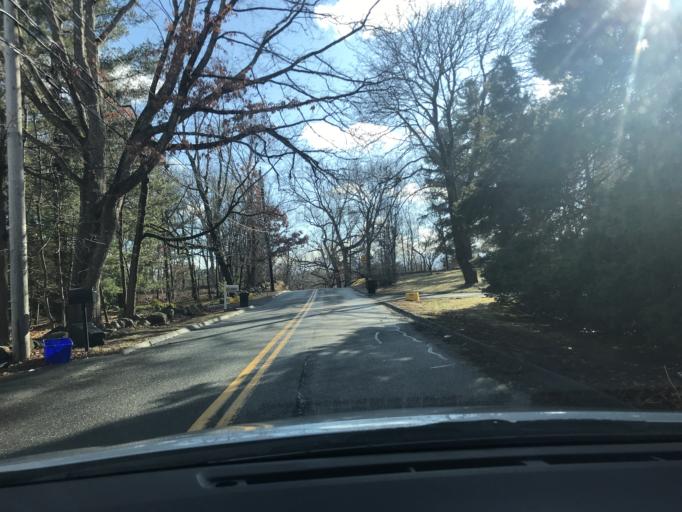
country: US
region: Massachusetts
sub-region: Middlesex County
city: Lexington
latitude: 42.4709
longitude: -71.2185
